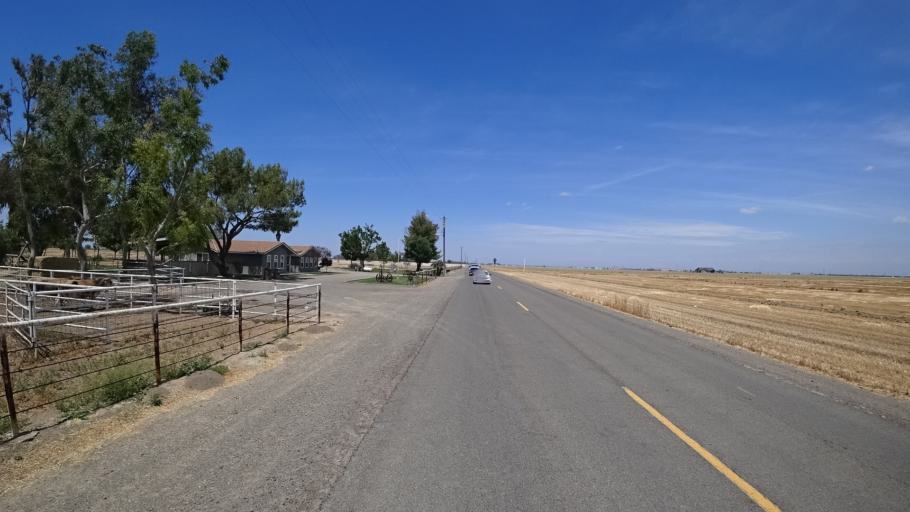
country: US
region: California
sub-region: Kings County
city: Home Garden
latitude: 36.2283
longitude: -119.6729
